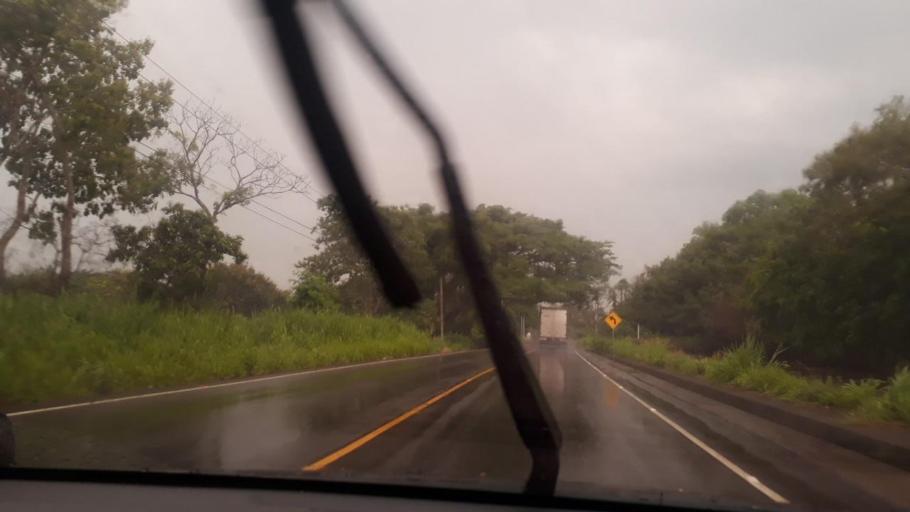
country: GT
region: Santa Rosa
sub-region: Municipio de Taxisco
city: Taxisco
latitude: 14.0901
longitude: -90.5091
